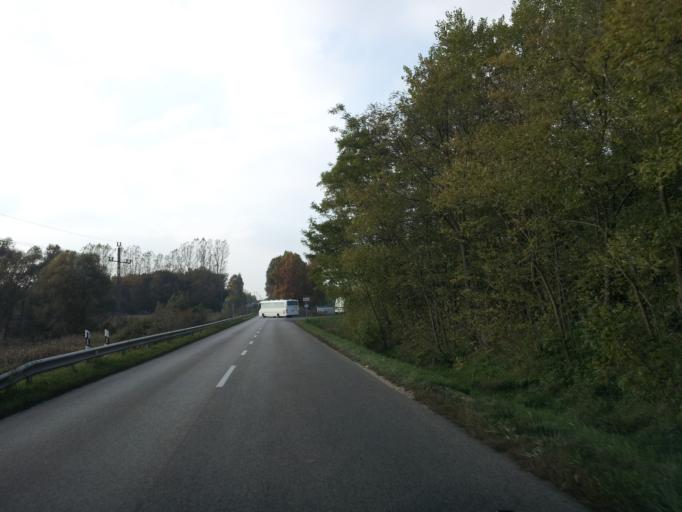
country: HU
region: Komarom-Esztergom
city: Bokod
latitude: 47.4867
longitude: 18.2670
